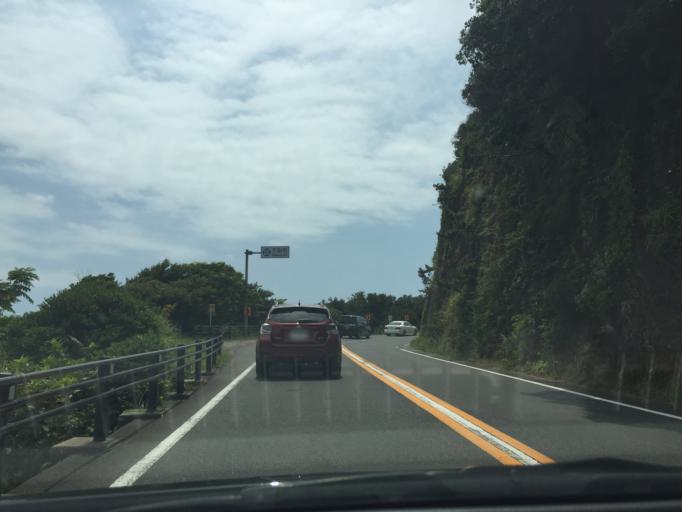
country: JP
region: Shizuoka
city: Shimoda
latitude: 34.7179
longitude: 138.9911
